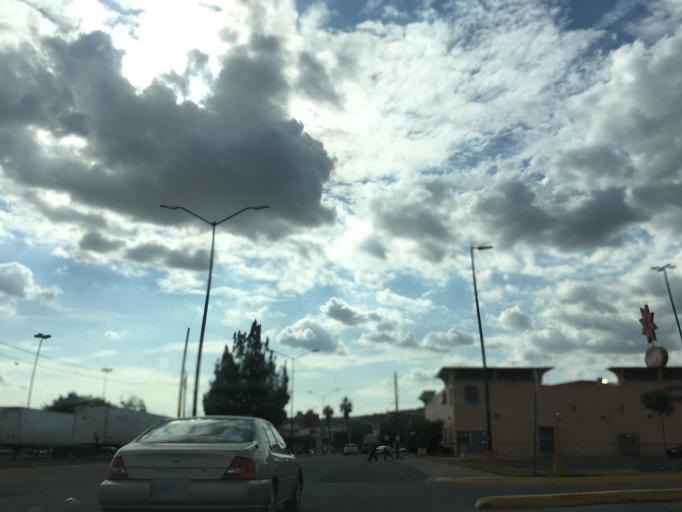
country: MX
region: Guanajuato
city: Leon
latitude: 21.1604
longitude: -101.6910
